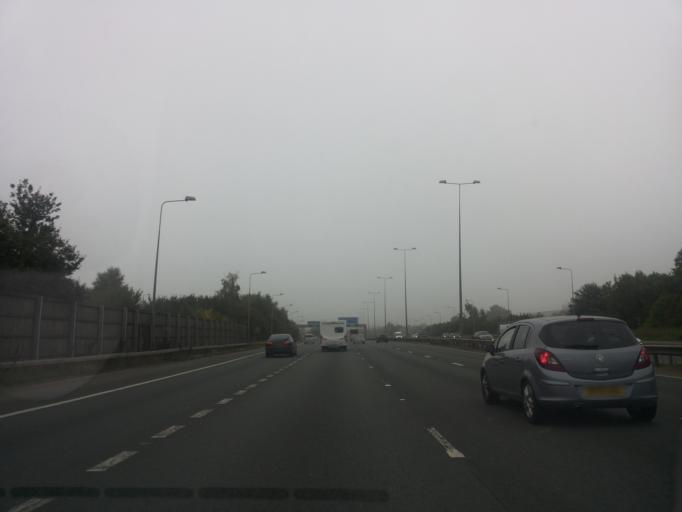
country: GB
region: England
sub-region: Borough of Tameside
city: Droylsden
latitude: 53.4752
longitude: -2.1266
